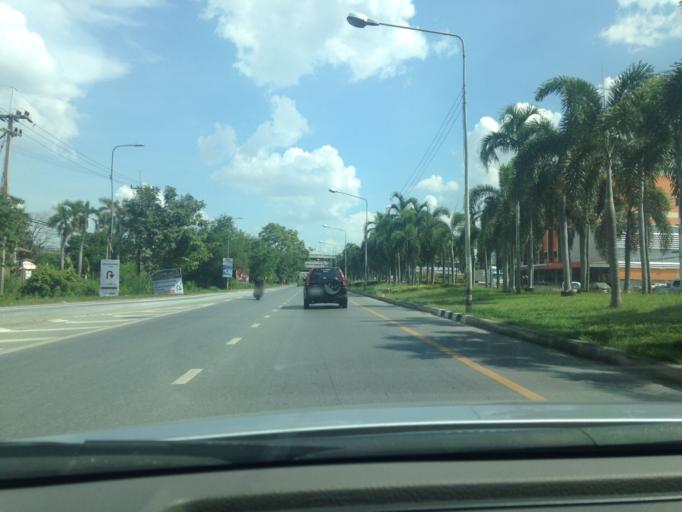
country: TH
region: Phra Nakhon Si Ayutthaya
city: Ban Bang Kadi Pathum Thani
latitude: 14.0040
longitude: 100.5661
